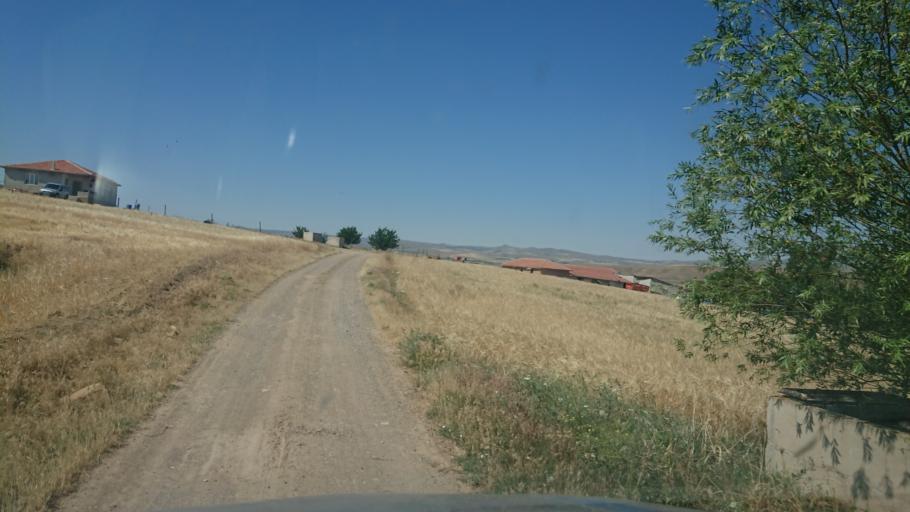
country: TR
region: Ankara
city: Evren
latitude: 39.0520
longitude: 33.8783
